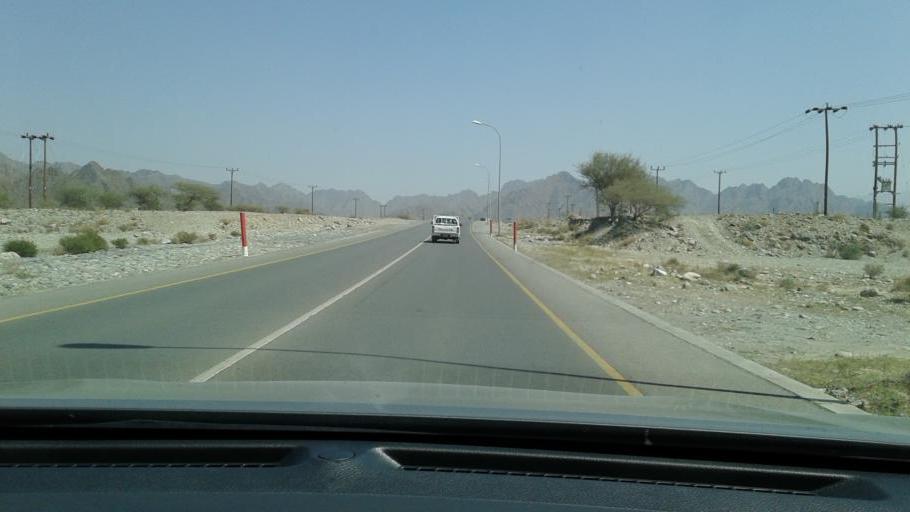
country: OM
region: Al Batinah
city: Rustaq
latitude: 23.3677
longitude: 57.4640
